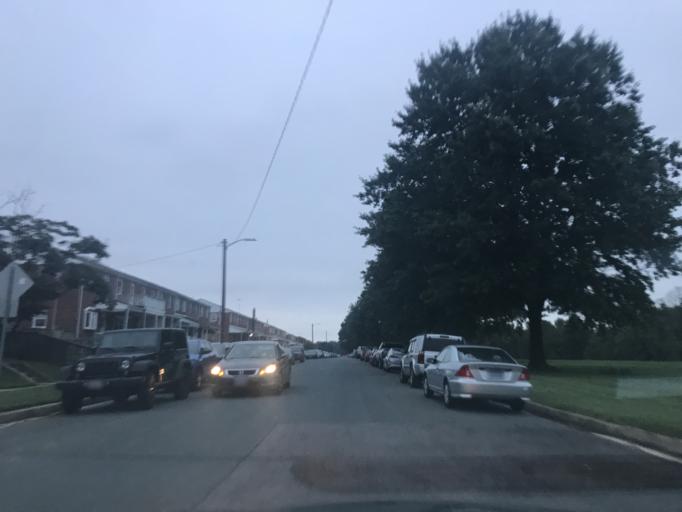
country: US
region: Maryland
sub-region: Baltimore County
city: Essex
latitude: 39.2700
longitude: -76.4831
